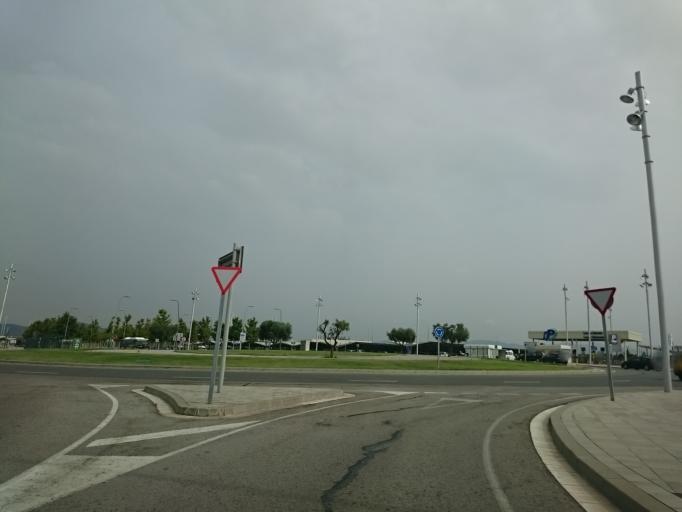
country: ES
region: Catalonia
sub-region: Provincia de Barcelona
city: Viladecans
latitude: 41.2908
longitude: 2.0552
